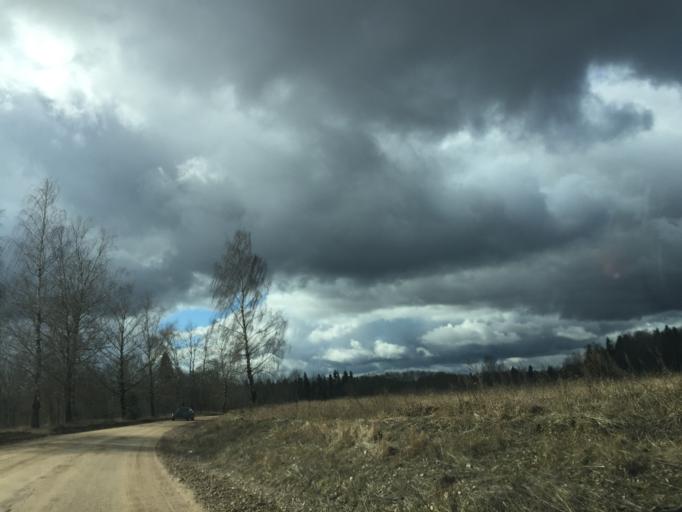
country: LV
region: Akniste
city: Akniste
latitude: 56.1107
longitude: 25.8805
